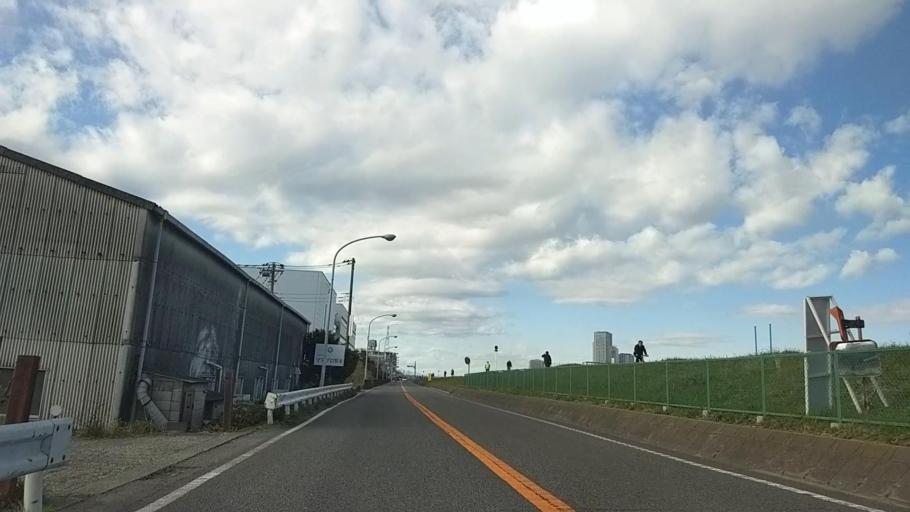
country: JP
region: Kanagawa
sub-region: Kawasaki-shi
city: Kawasaki
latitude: 35.5954
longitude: 139.6430
